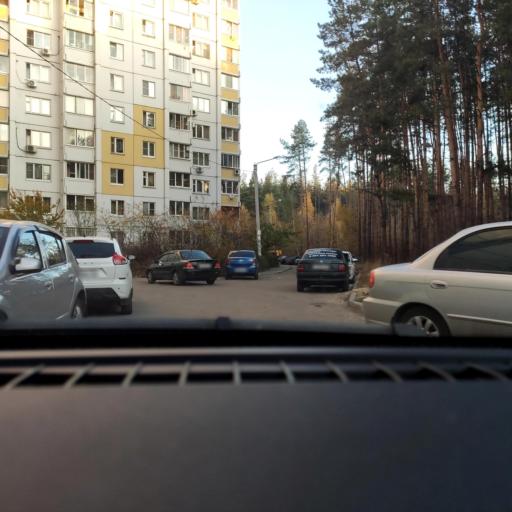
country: RU
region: Voronezj
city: Somovo
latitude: 51.6915
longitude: 39.2819
